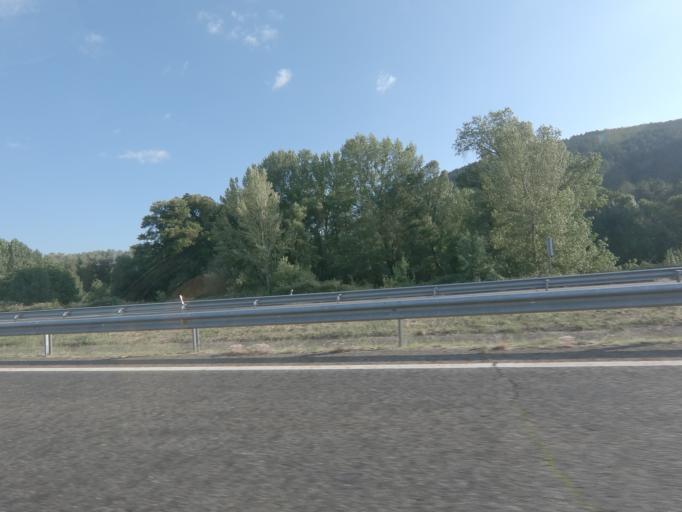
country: ES
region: Galicia
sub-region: Provincia de Ourense
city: Verin
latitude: 41.9179
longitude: -7.4520
